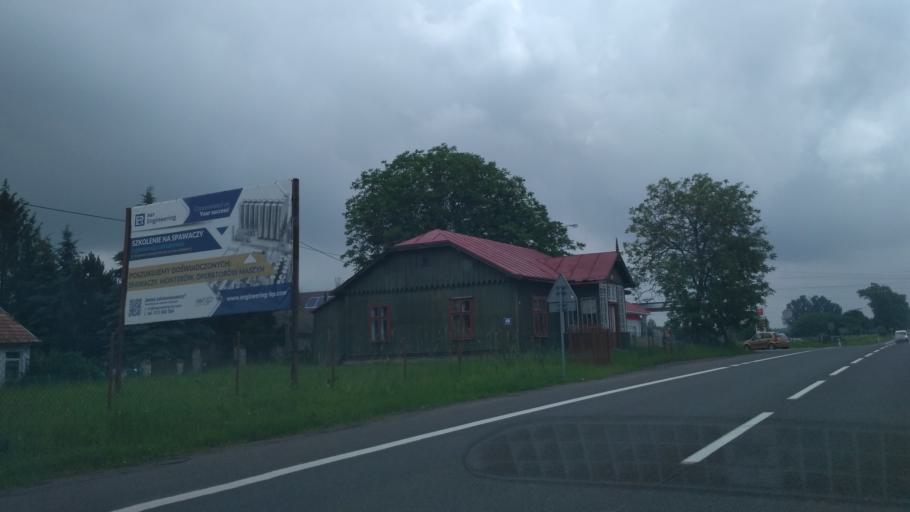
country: PL
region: Subcarpathian Voivodeship
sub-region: Powiat przeworski
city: Przeworsk
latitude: 50.0553
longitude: 22.5091
